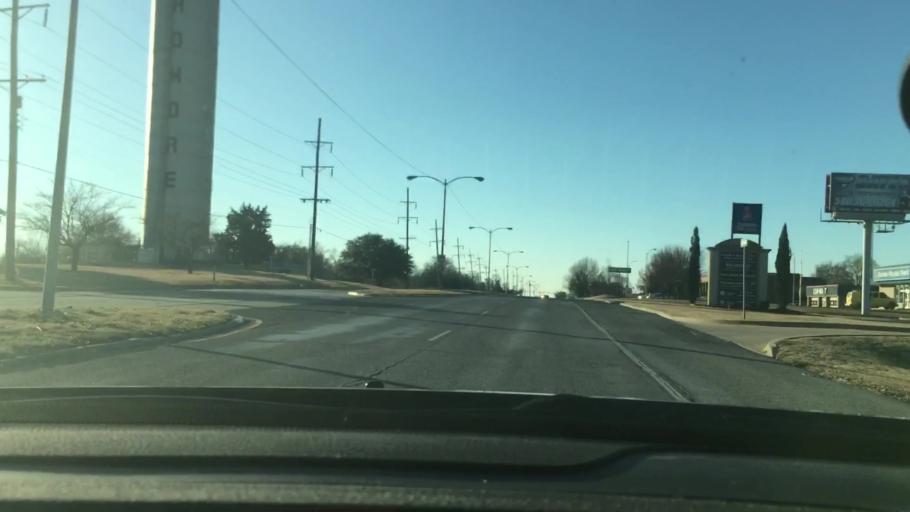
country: US
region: Oklahoma
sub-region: Carter County
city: Ardmore
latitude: 34.1993
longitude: -97.1432
